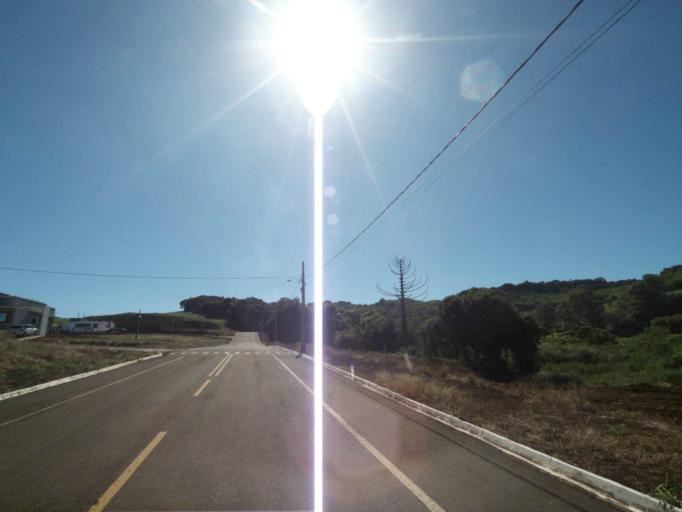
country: BR
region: Parana
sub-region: Pato Branco
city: Pato Branco
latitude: -26.2640
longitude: -52.7745
